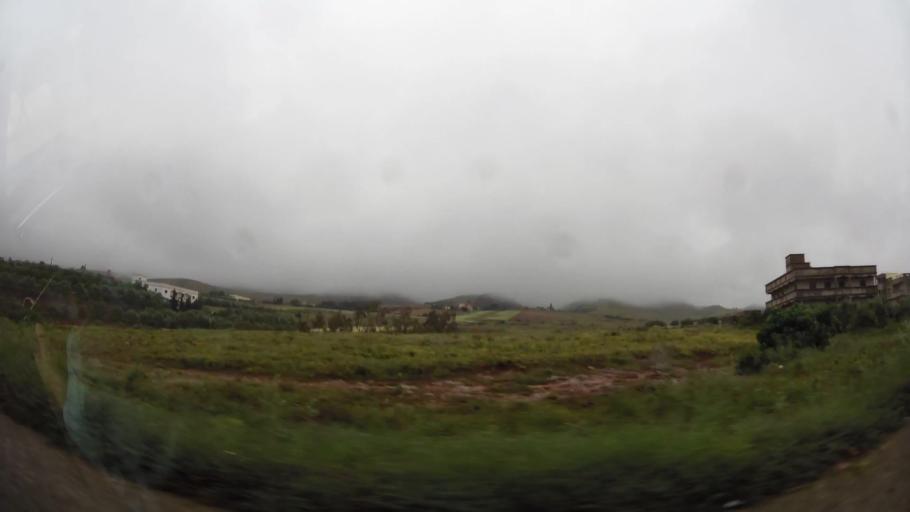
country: MA
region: Oriental
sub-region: Nador
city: Boudinar
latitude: 35.1181
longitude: -3.5762
